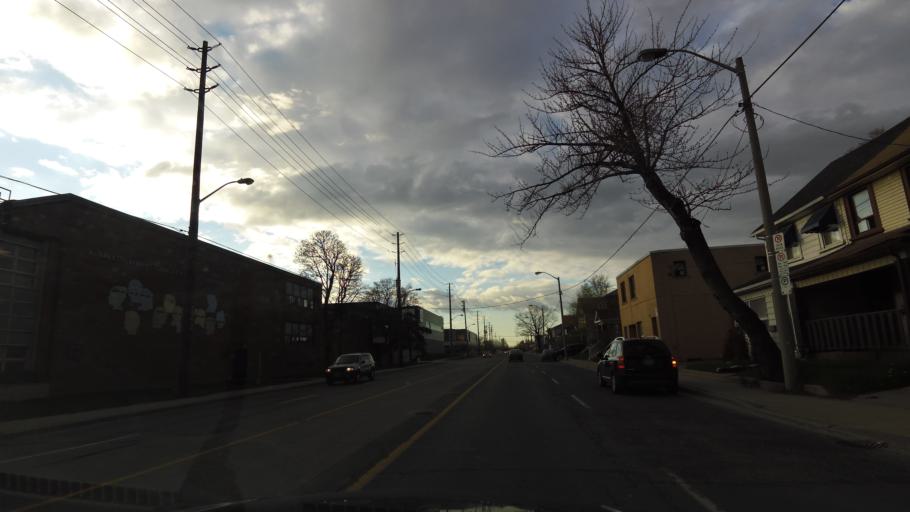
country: CA
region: Ontario
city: Etobicoke
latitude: 43.6015
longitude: -79.5184
